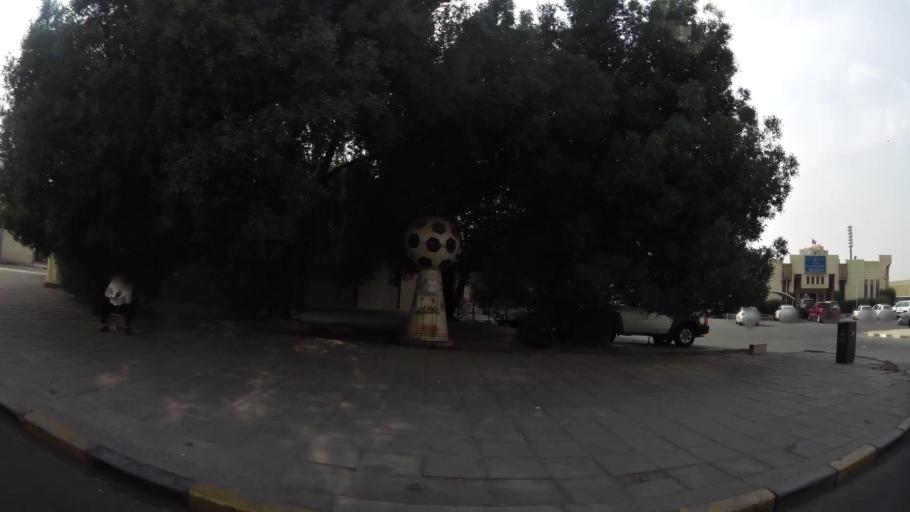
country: KW
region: Al Farwaniyah
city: Al Farwaniyah
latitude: 29.2806
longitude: 47.9608
